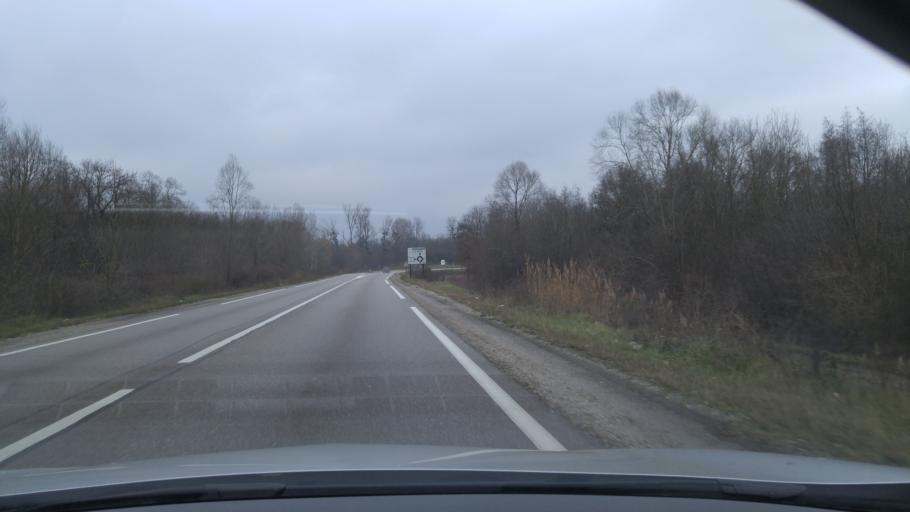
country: FR
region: Rhone-Alpes
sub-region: Departement de l'Isere
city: La Verpilliere
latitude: 45.6395
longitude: 5.1551
